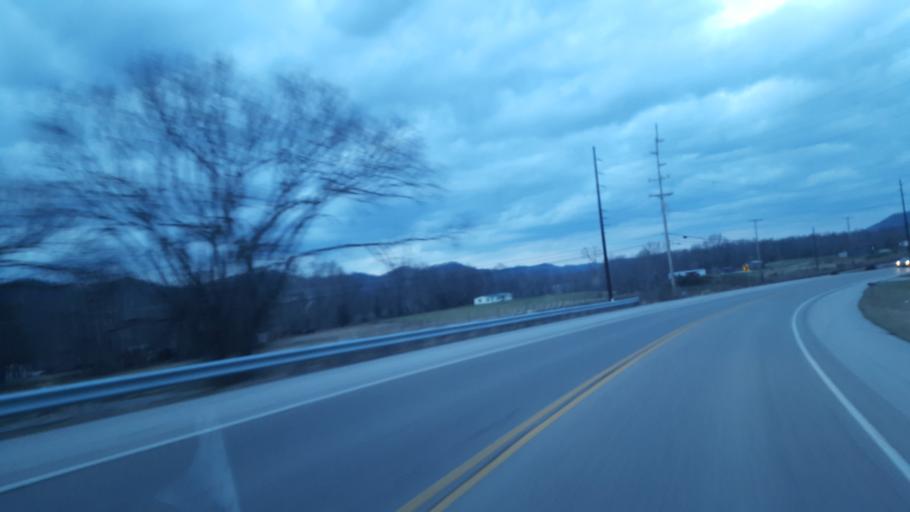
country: US
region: Kentucky
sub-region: Lewis County
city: Vanceburg
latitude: 38.6174
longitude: -83.1426
